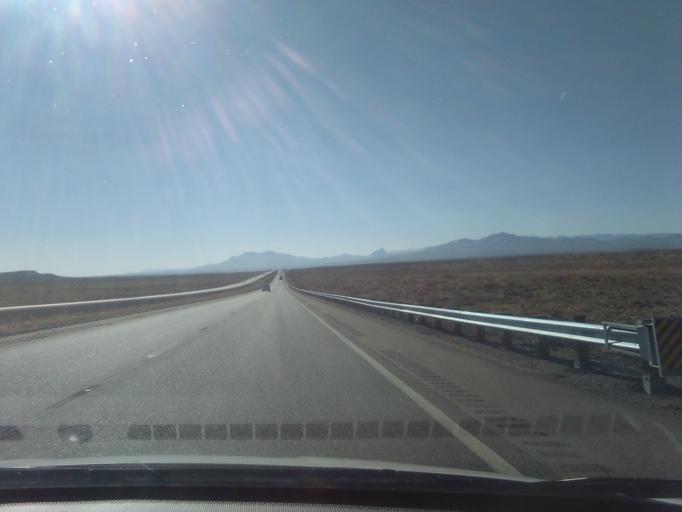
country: US
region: New Mexico
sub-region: Socorro County
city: Socorro
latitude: 34.3017
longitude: -106.8912
